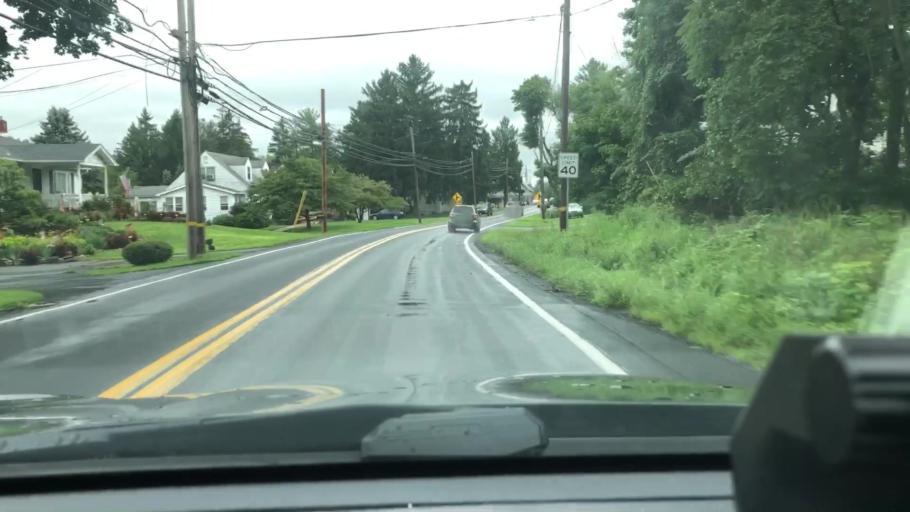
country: US
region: Pennsylvania
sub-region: Lehigh County
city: Coopersburg
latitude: 40.5214
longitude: -75.3907
